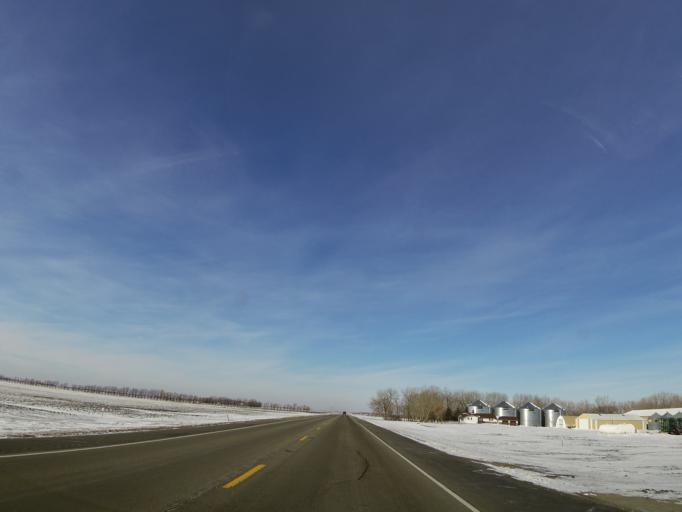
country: US
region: North Dakota
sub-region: Walsh County
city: Grafton
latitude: 48.4121
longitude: -97.2164
